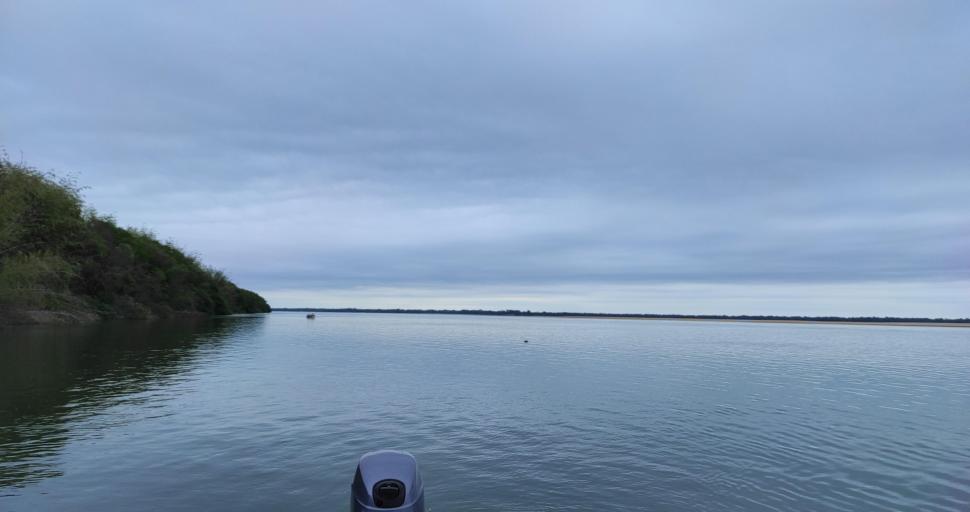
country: PY
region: Neembucu
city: Cerrito
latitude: -27.3434
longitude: -57.7070
